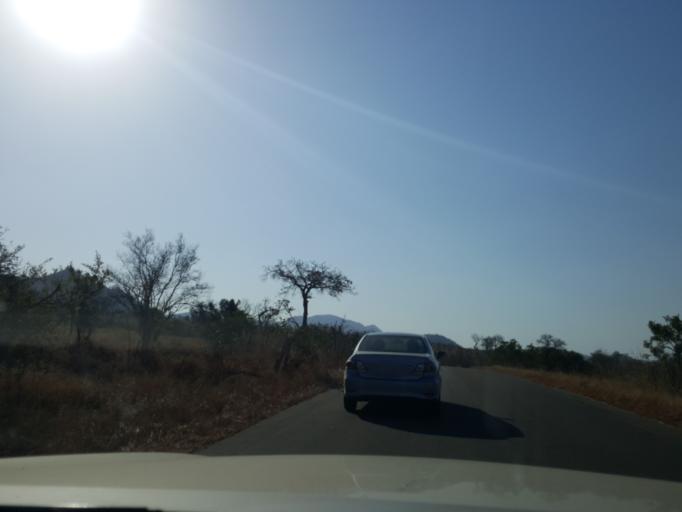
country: SZ
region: Hhohho
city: Ntfonjeni
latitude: -25.4350
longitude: 31.4436
